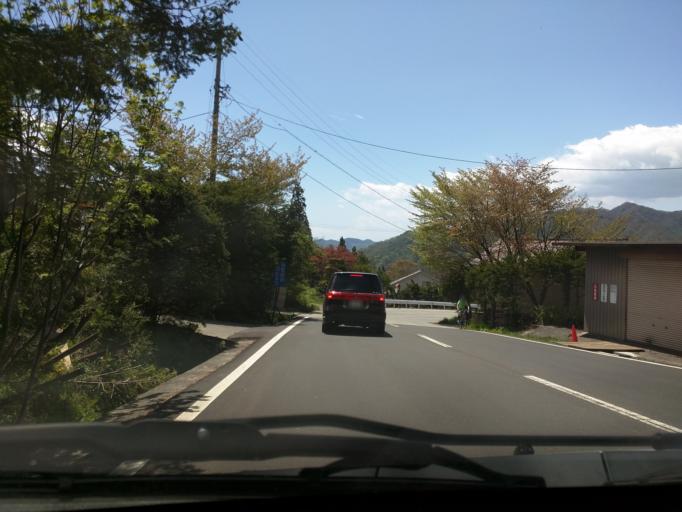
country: JP
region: Nagano
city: Nagano-shi
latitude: 36.7318
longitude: 138.0790
